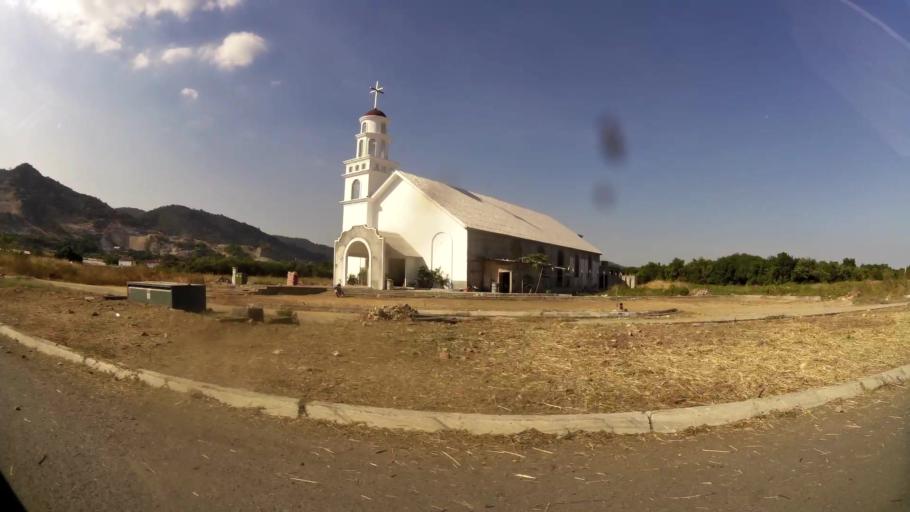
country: EC
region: Guayas
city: Santa Lucia
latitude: -2.1906
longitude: -80.0010
